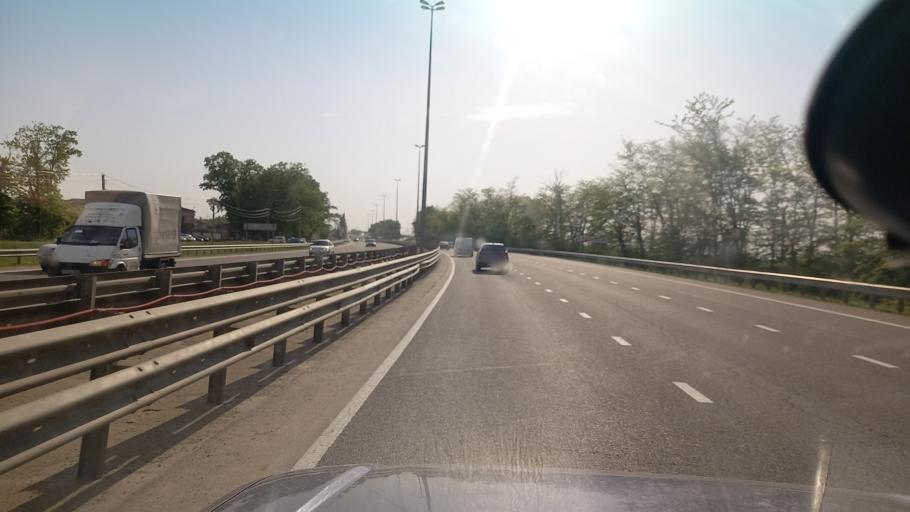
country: RU
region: Krasnodarskiy
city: Yelizavetinskaya
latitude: 45.0568
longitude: 38.8678
